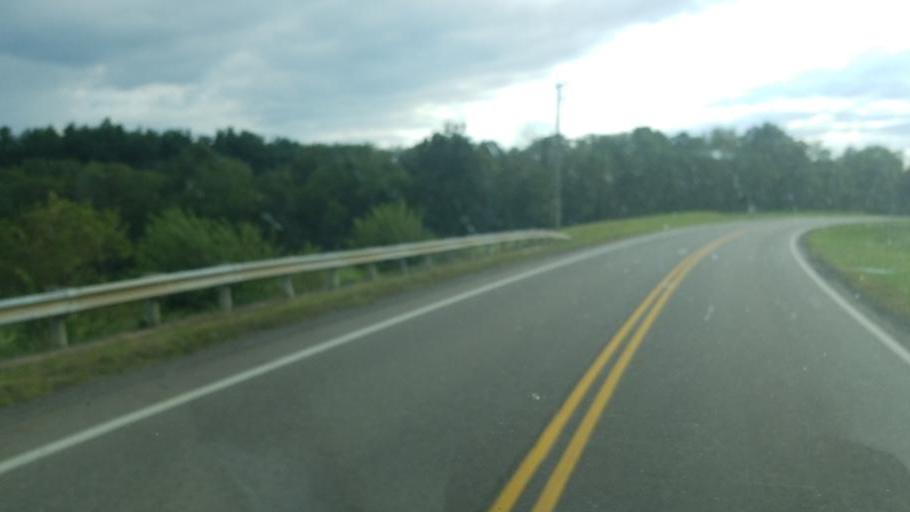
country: US
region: Ohio
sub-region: Knox County
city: Danville
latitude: 40.4523
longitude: -82.2369
